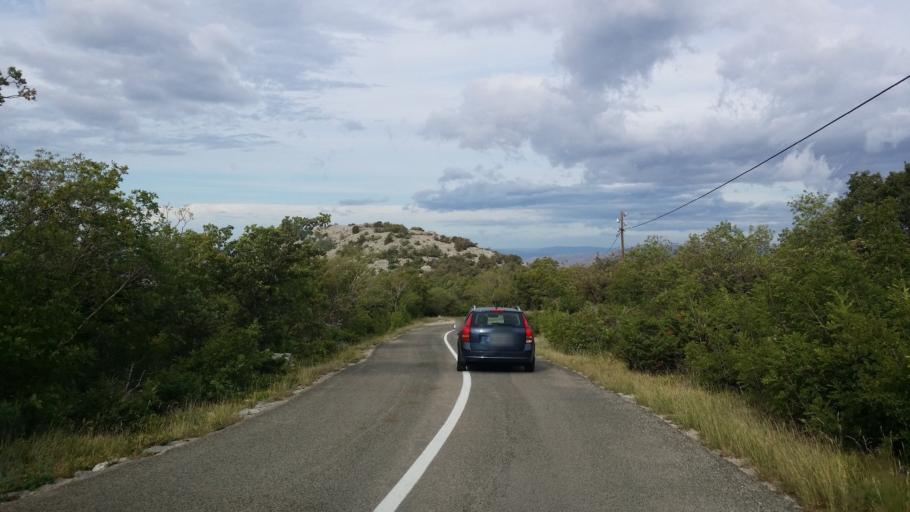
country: HR
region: Licko-Senjska
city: Senj
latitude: 44.9085
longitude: 14.9456
